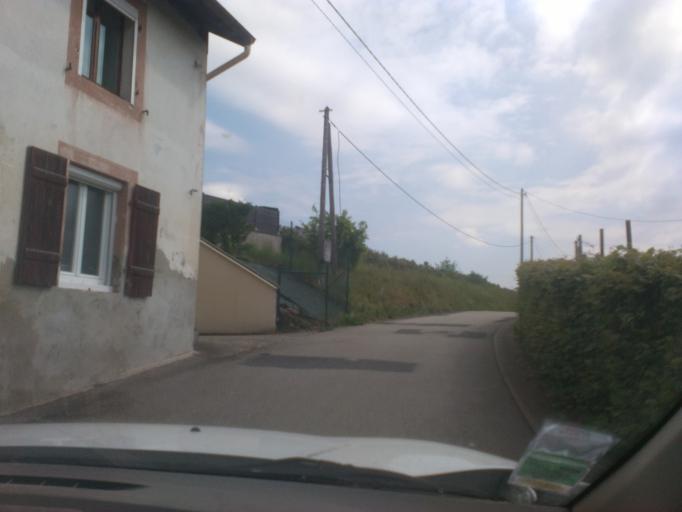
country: FR
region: Lorraine
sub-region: Departement des Vosges
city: Moyenmoutier
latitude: 48.3849
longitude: 6.9319
